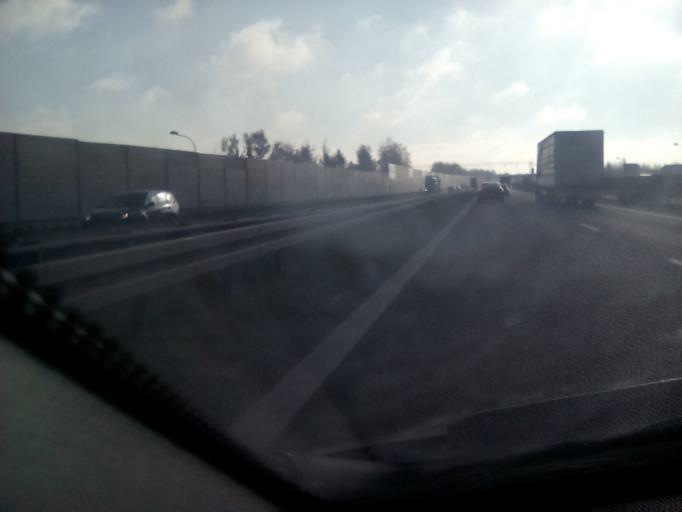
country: PL
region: Masovian Voivodeship
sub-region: Powiat grojecki
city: Grojec
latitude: 51.8584
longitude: 20.8589
